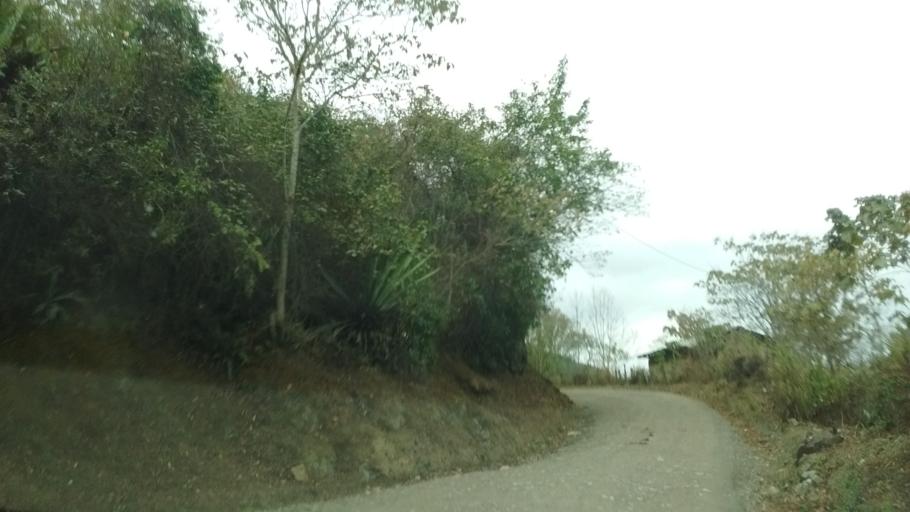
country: CO
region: Cauca
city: Almaguer
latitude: 1.8617
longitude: -76.9334
